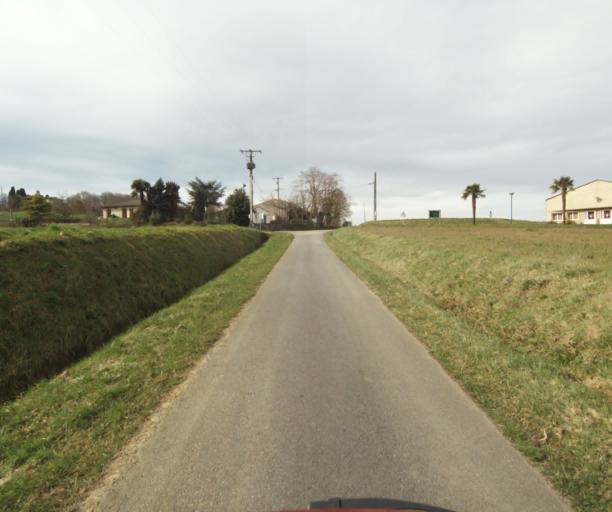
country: FR
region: Midi-Pyrenees
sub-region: Departement de l'Ariege
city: Verniolle
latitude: 43.0598
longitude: 1.7359
